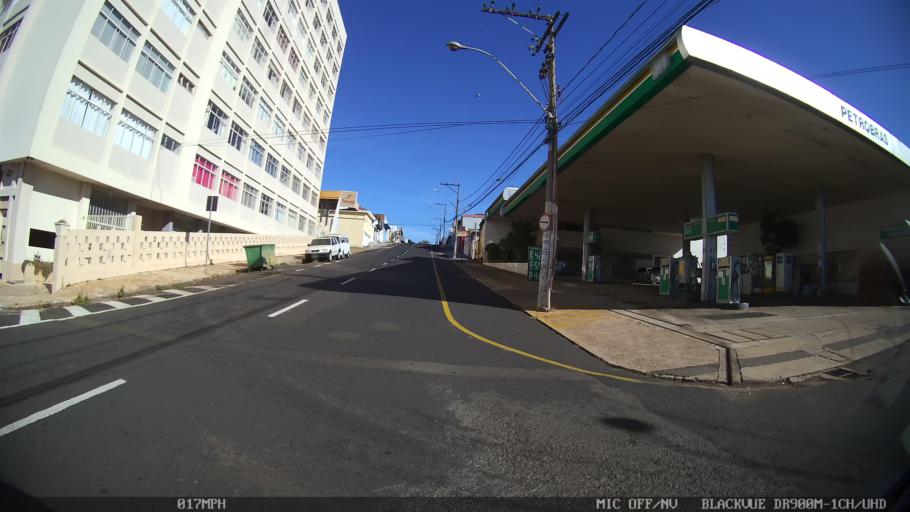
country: BR
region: Sao Paulo
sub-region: Franca
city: Franca
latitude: -20.5336
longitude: -47.4084
